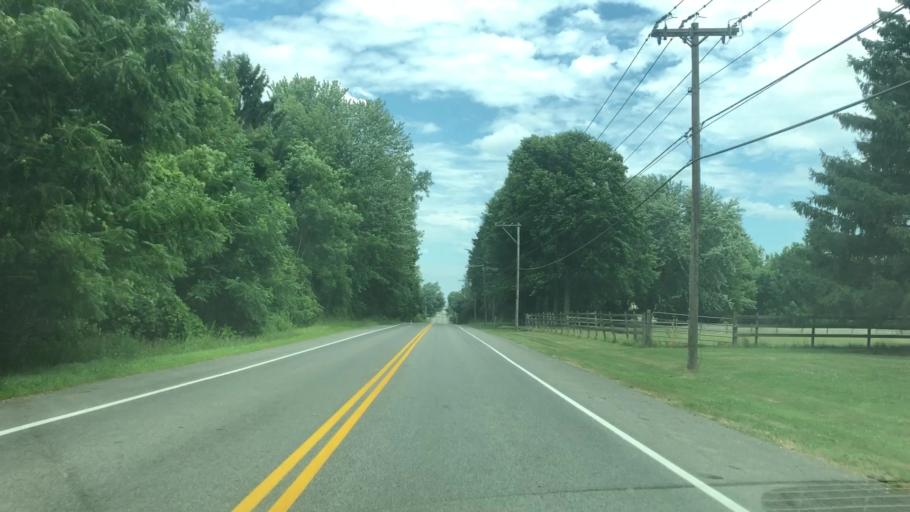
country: US
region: New York
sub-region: Monroe County
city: Fairport
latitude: 43.1319
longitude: -77.4005
